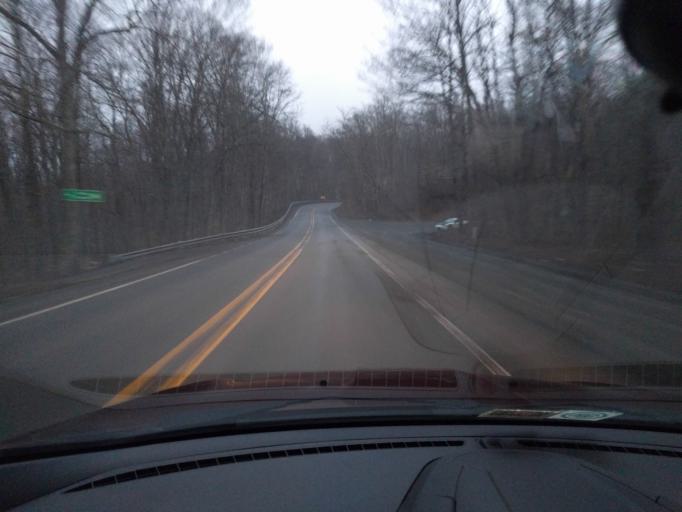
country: US
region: West Virginia
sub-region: Greenbrier County
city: Rainelle
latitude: 37.9816
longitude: -80.8393
